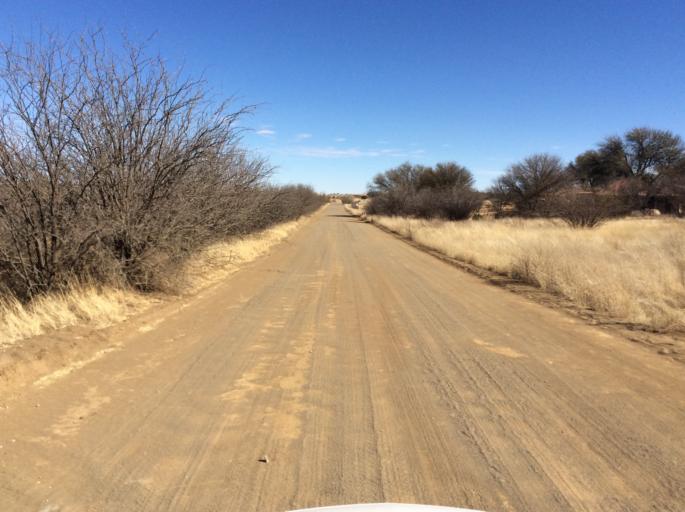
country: ZA
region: Orange Free State
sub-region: Lejweleputswa District Municipality
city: Brandfort
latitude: -28.7238
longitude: 26.0643
